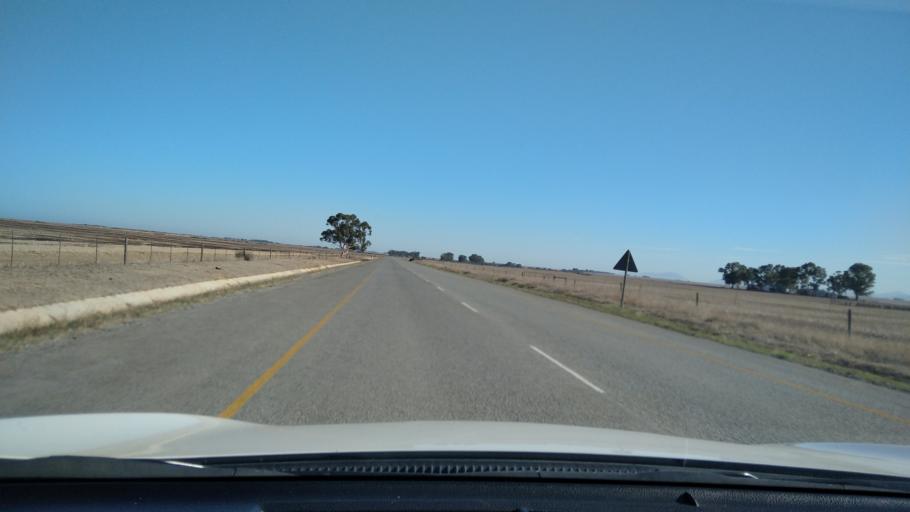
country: ZA
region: Western Cape
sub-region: West Coast District Municipality
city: Moorreesburg
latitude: -33.2866
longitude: 18.6063
